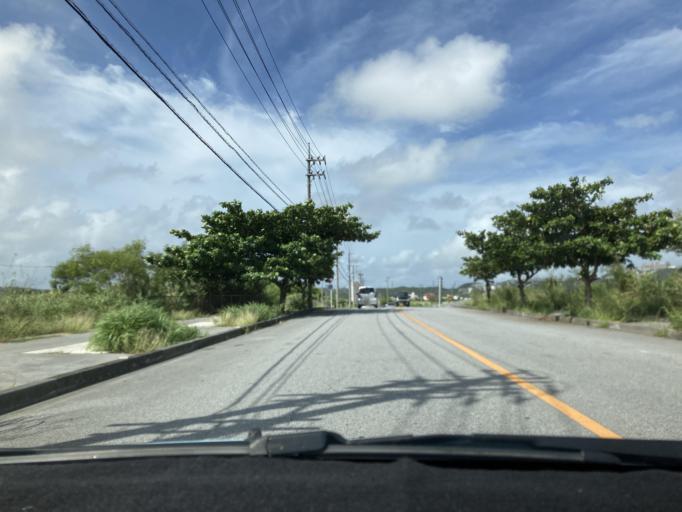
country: JP
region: Okinawa
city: Ginowan
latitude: 26.2205
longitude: 127.7754
